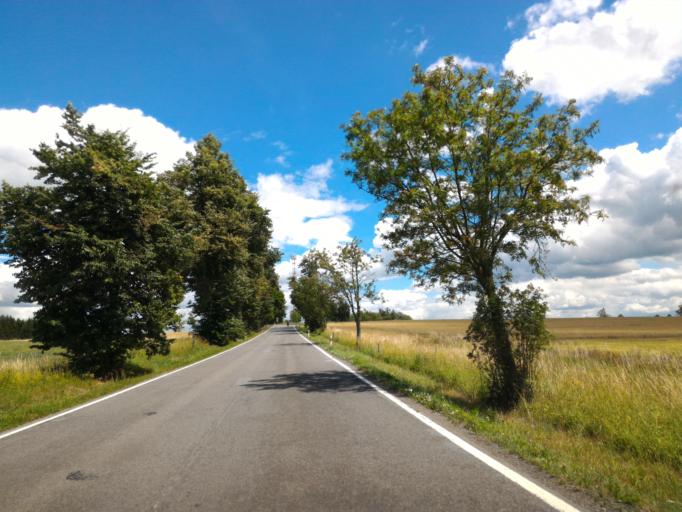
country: CZ
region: Vysocina
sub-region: Okres Jihlava
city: Polna
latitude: 49.4405
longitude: 15.7379
